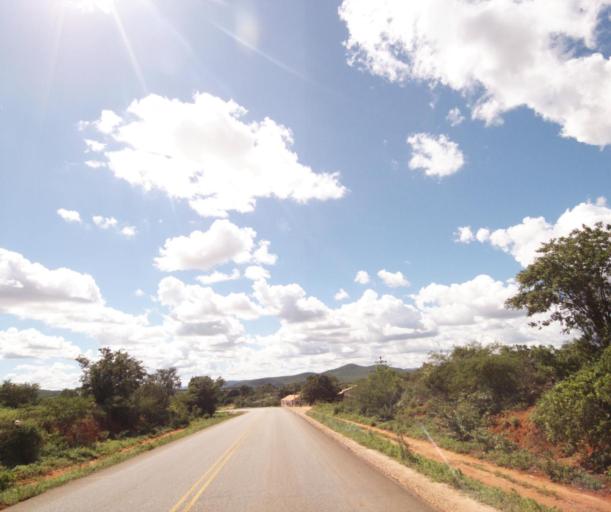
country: BR
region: Bahia
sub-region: Caetite
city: Caetite
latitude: -14.1722
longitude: -42.1862
